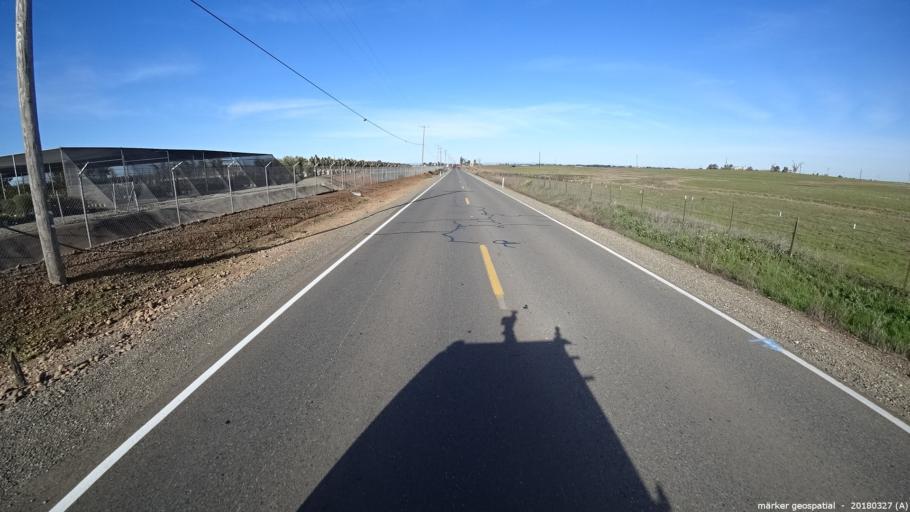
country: US
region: California
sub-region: Sacramento County
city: Vineyard
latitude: 38.4962
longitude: -121.2941
